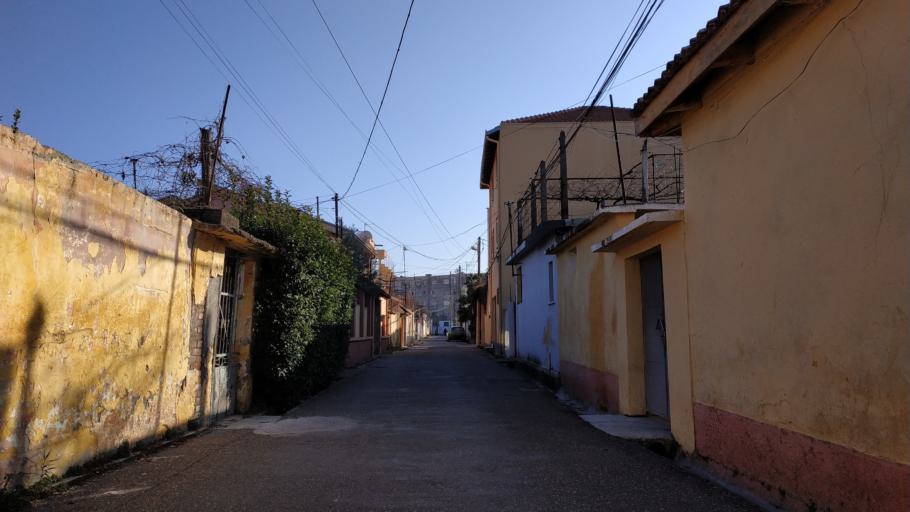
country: AL
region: Shkoder
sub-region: Rrethi i Shkodres
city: Shkoder
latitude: 42.0633
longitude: 19.5226
